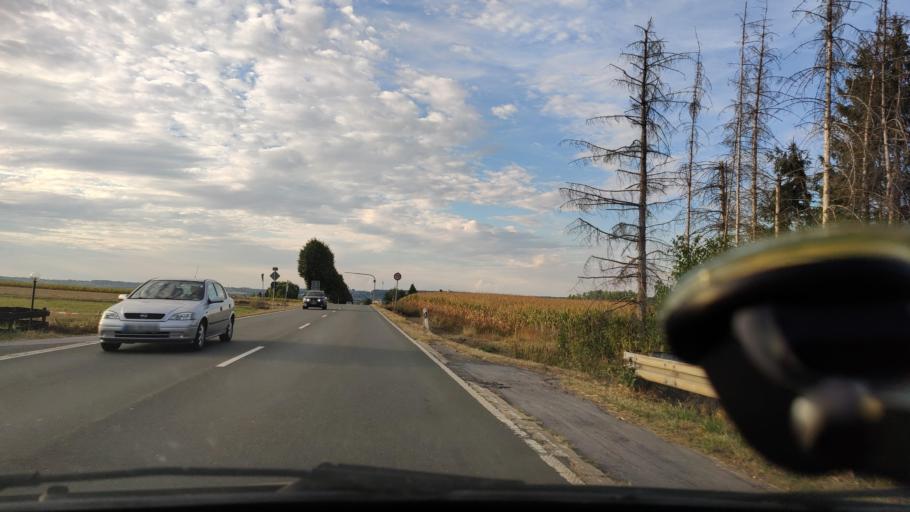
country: DE
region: North Rhine-Westphalia
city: Schwerte
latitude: 51.4050
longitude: 7.5778
